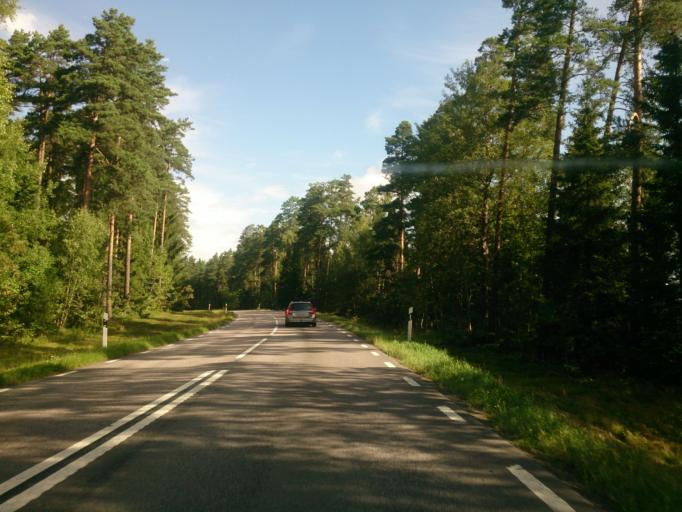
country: SE
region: OEstergoetland
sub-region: Atvidabergs Kommun
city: Atvidaberg
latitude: 58.2650
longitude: 15.9246
